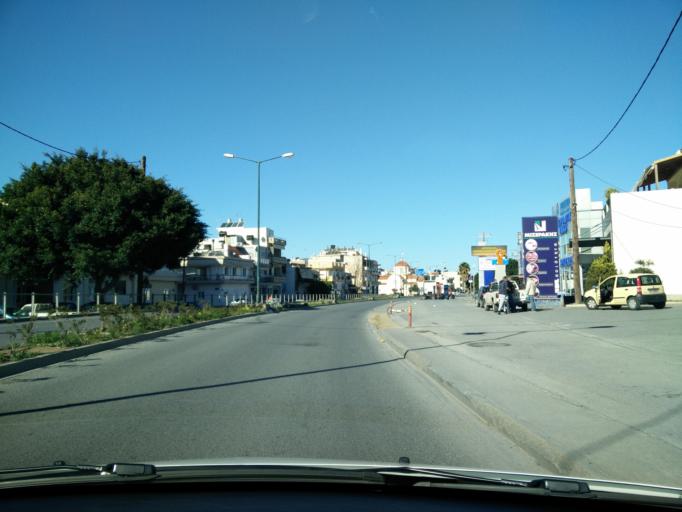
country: GR
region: Crete
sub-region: Nomos Irakleiou
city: Nea Alikarnassos
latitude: 35.3376
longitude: 25.1543
